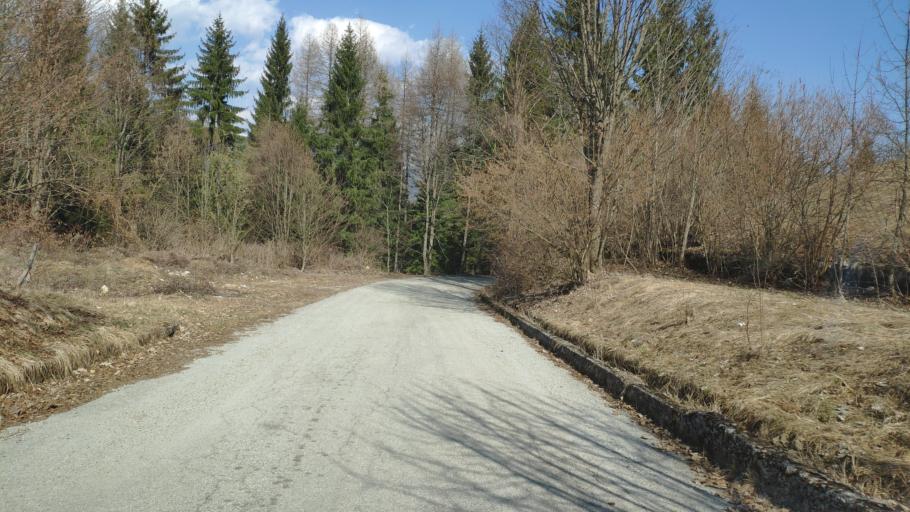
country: IT
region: Veneto
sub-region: Provincia di Vicenza
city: Enego
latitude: 45.9577
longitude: 11.6818
